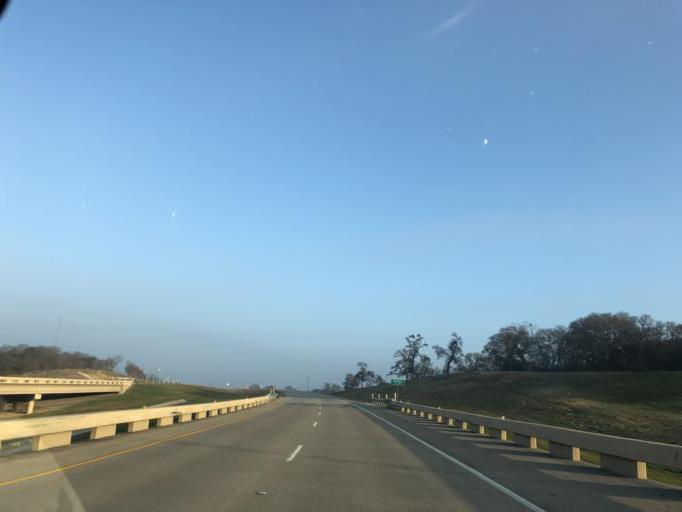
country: US
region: Texas
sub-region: Dallas County
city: Cedar Hill
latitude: 32.6368
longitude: -96.9721
